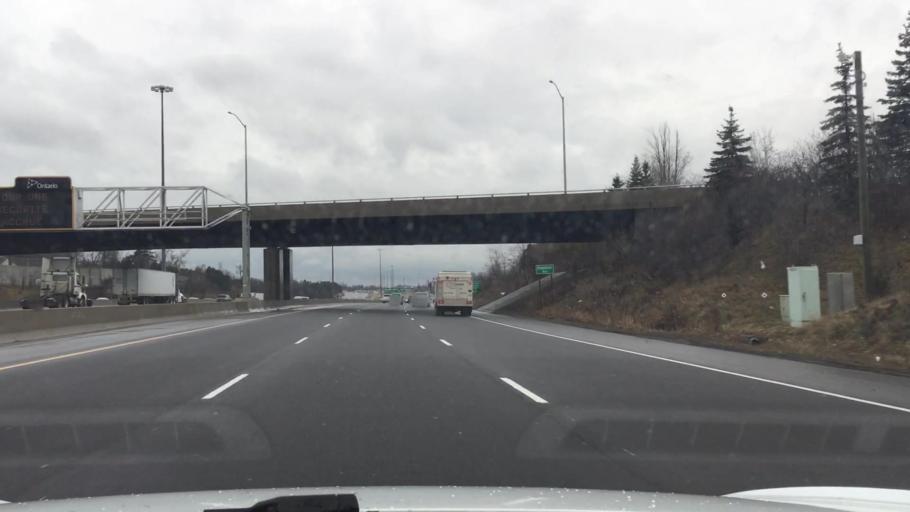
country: CA
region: Ontario
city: Pickering
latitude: 43.8083
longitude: -79.1232
